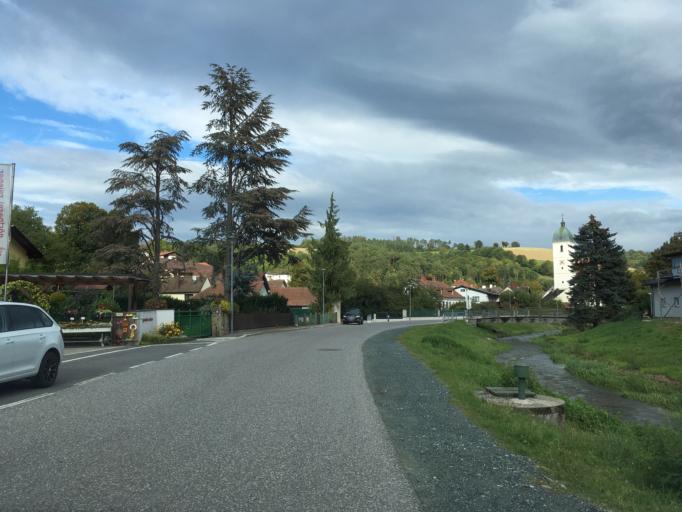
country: AT
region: Lower Austria
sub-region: Politischer Bezirk Wiener Neustadt
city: Kirchschlag in der Buckligen Welt
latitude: 47.5025
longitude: 16.2926
